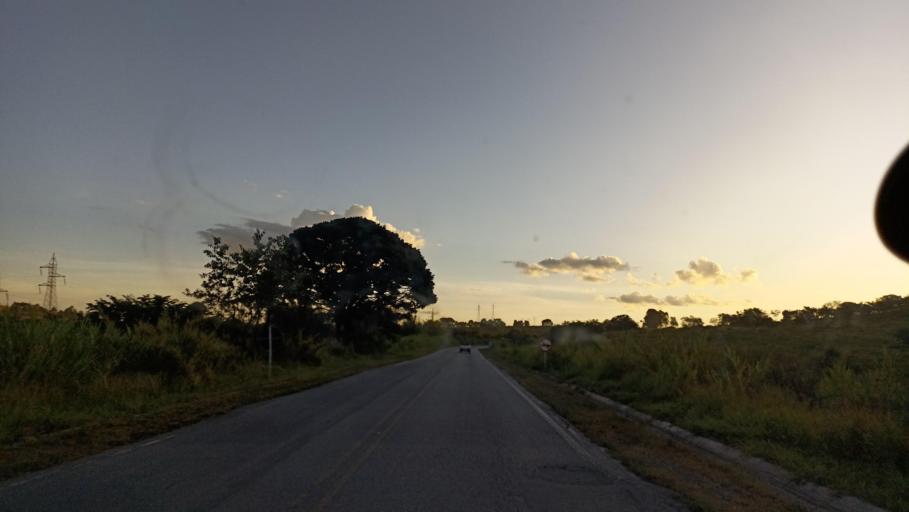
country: BR
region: Minas Gerais
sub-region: Sao Joao Del Rei
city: Sao Joao del Rei
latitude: -21.2333
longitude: -44.3872
